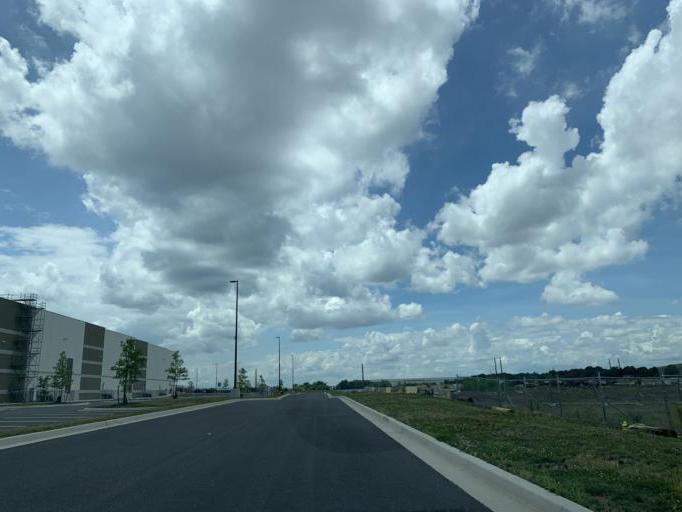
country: US
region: Maryland
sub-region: Baltimore County
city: Edgemere
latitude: 39.2336
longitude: -76.4692
